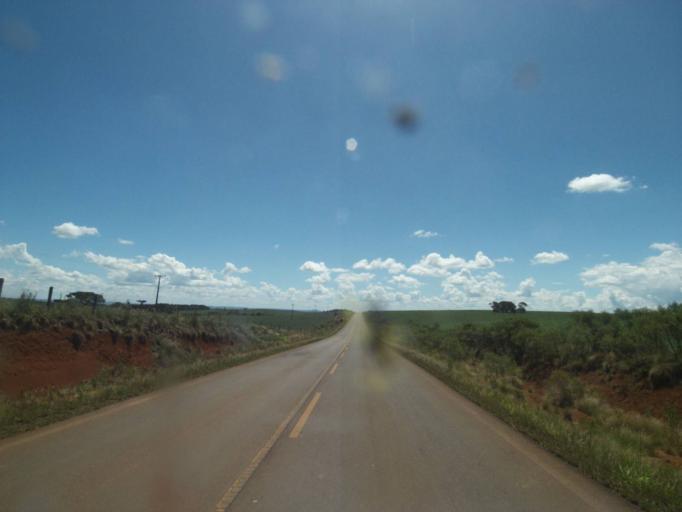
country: BR
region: Parana
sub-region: Pinhao
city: Pinhao
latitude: -25.8132
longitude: -52.0551
